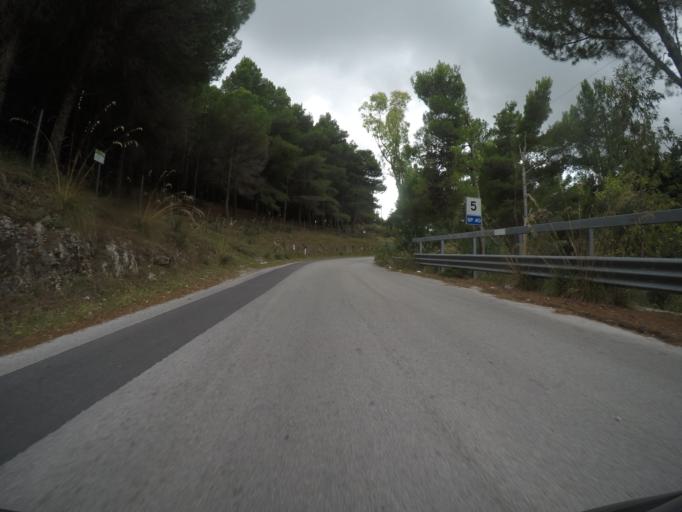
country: IT
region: Sicily
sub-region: Palermo
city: Montelepre
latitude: 38.1145
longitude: 13.1662
